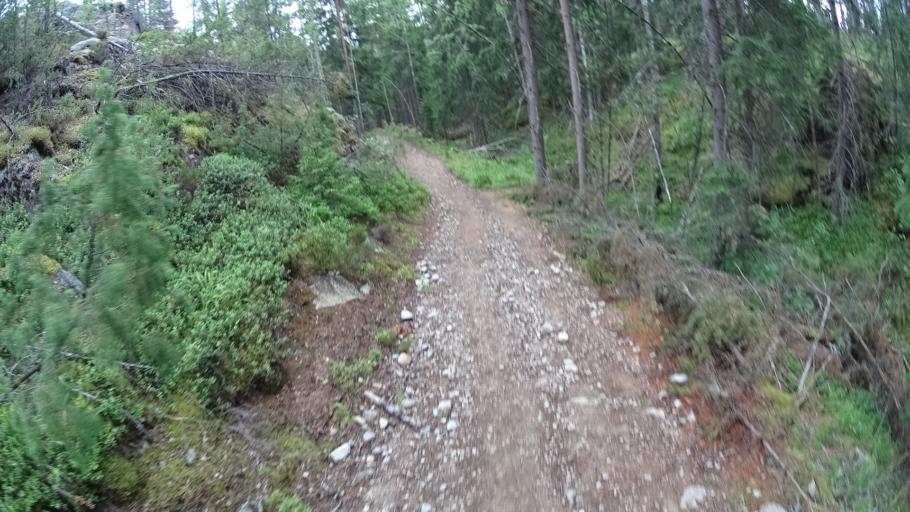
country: FI
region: Southern Savonia
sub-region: Mikkeli
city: Maentyharju
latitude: 61.1808
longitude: 26.8907
